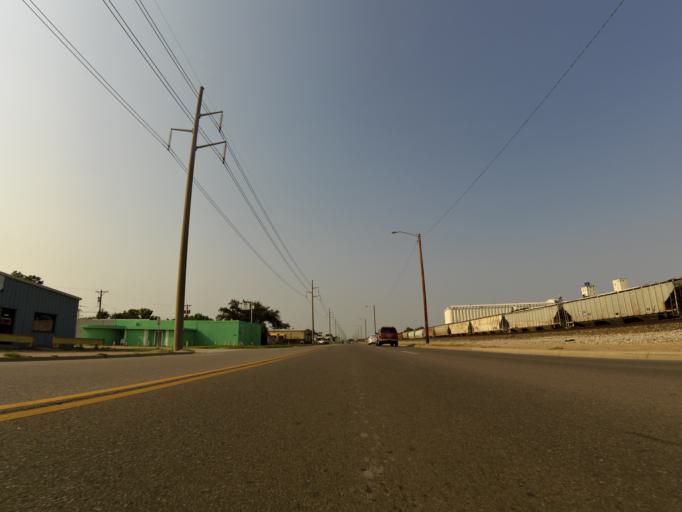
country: US
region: Kansas
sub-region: Sedgwick County
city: Wichita
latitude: 37.7390
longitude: -97.3359
